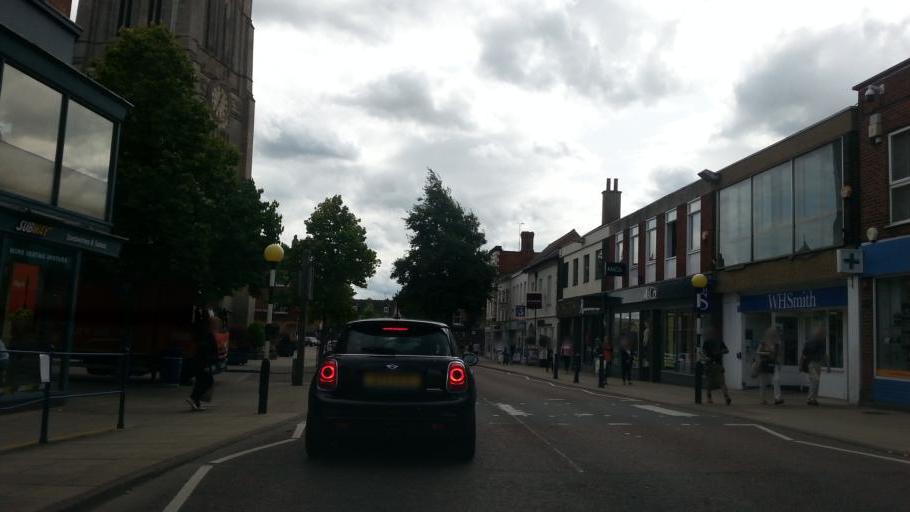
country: GB
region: England
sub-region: Leicestershire
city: Market Harborough
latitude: 52.4788
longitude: -0.9221
